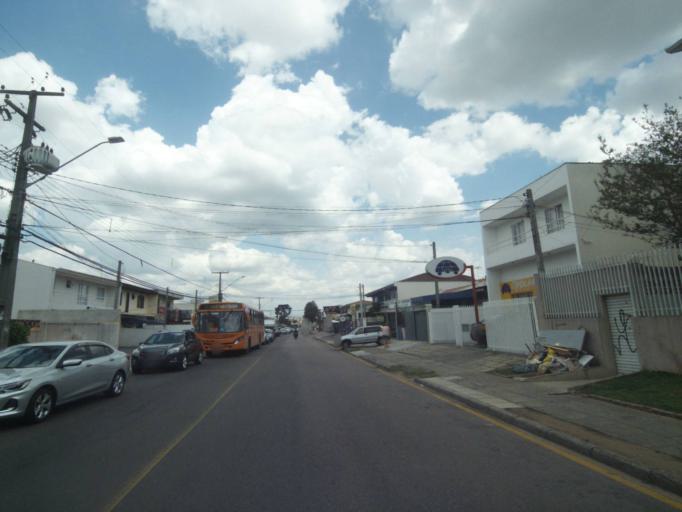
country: BR
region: Parana
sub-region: Sao Jose Dos Pinhais
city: Sao Jose dos Pinhais
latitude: -25.5368
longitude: -49.2728
